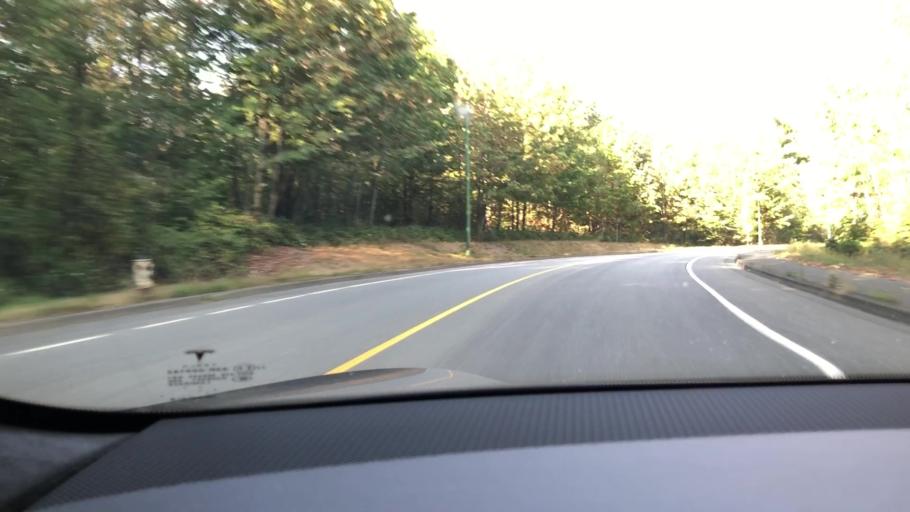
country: CA
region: British Columbia
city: Burnaby
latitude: 49.2294
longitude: -122.9764
